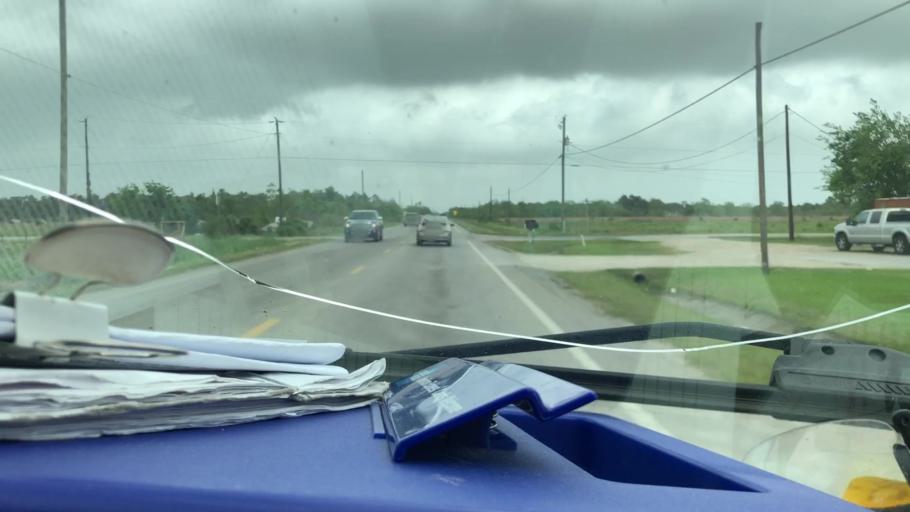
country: US
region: Texas
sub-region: Galveston County
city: Bacliff
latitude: 29.4766
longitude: -94.9712
